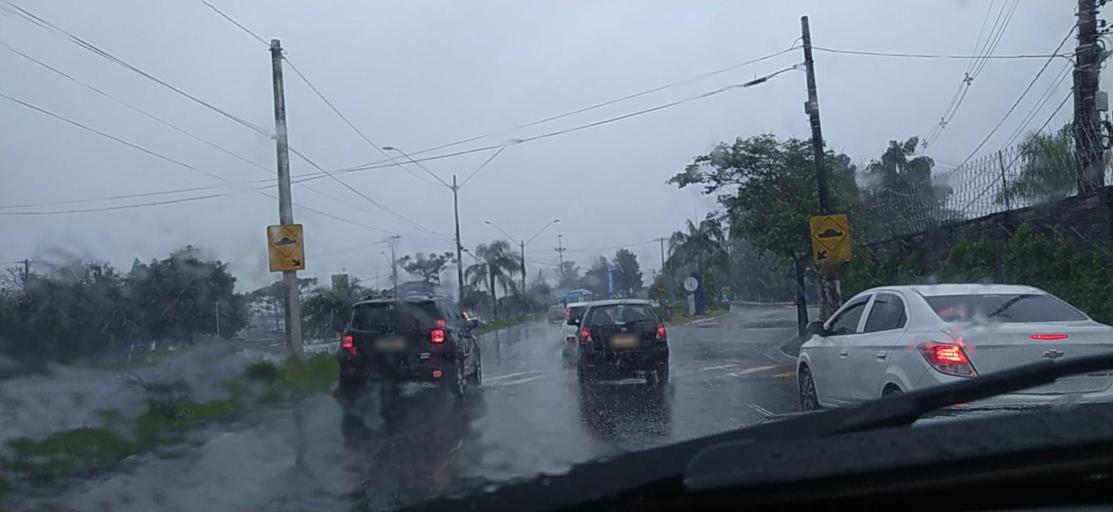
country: BR
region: Sao Paulo
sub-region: Jundiai
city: Jundiai
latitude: -23.1463
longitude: -46.9150
